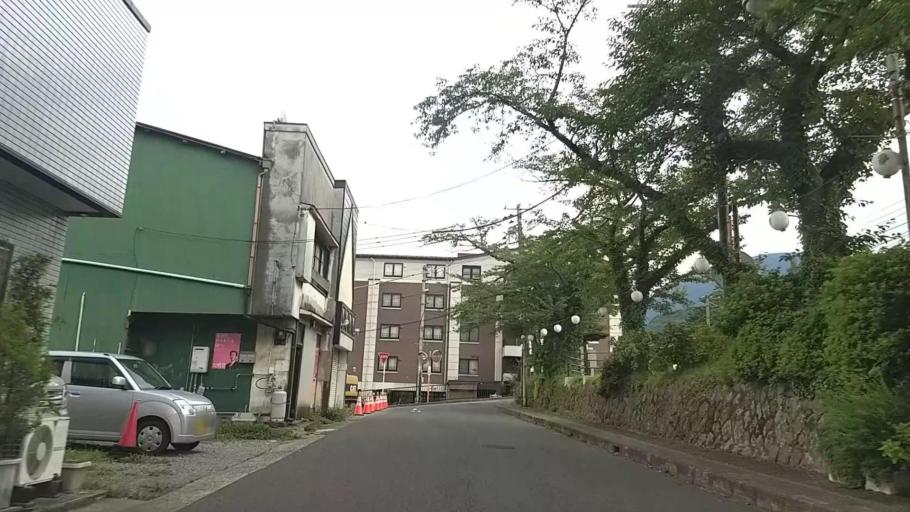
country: JP
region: Kanagawa
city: Hakone
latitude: 35.2505
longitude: 139.0486
